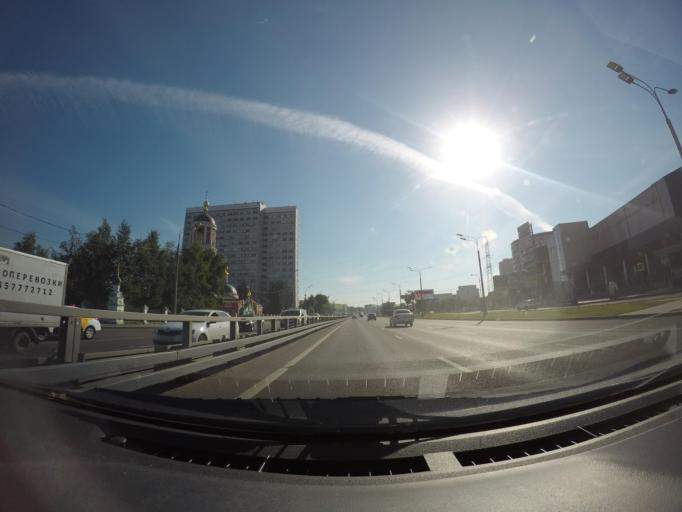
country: RU
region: Moscow
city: Tekstil'shchiki
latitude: 55.7310
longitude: 37.7310
